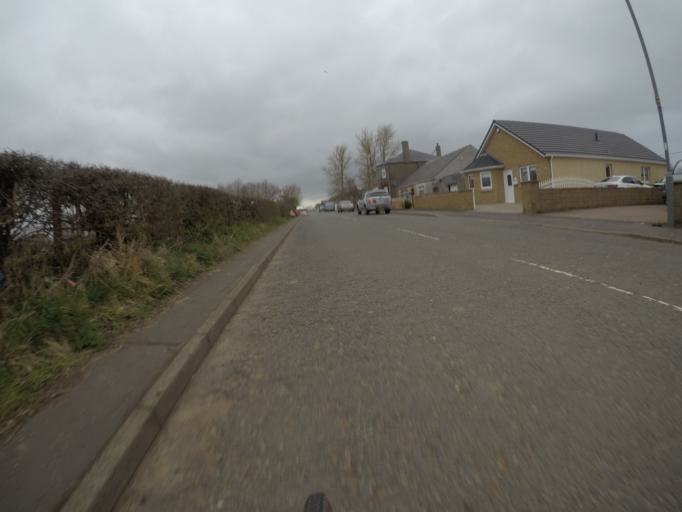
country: GB
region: Scotland
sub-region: North Ayrshire
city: Springside
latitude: 55.6174
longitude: -4.5903
